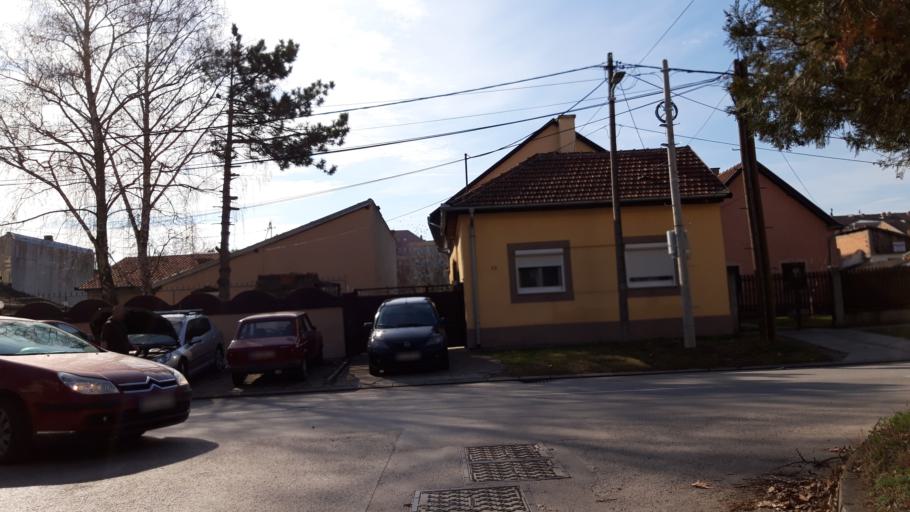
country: RS
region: Autonomna Pokrajina Vojvodina
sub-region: Juznobacki Okrug
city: Novi Sad
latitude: 45.2596
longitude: 19.8183
